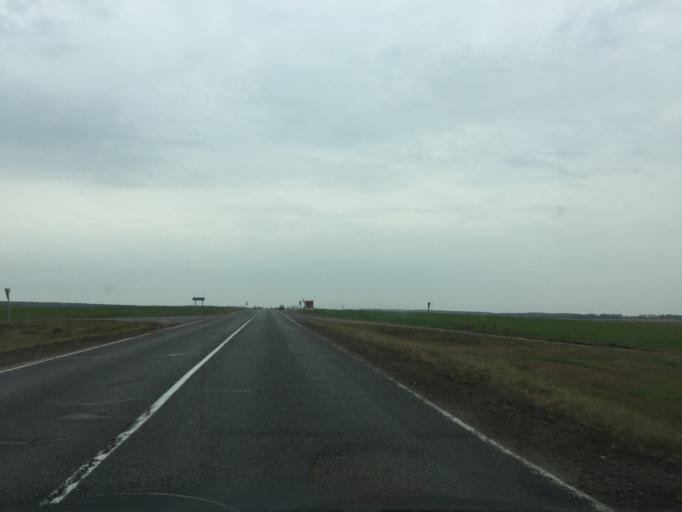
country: BY
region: Gomel
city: Dowsk
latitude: 53.1794
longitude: 30.4948
